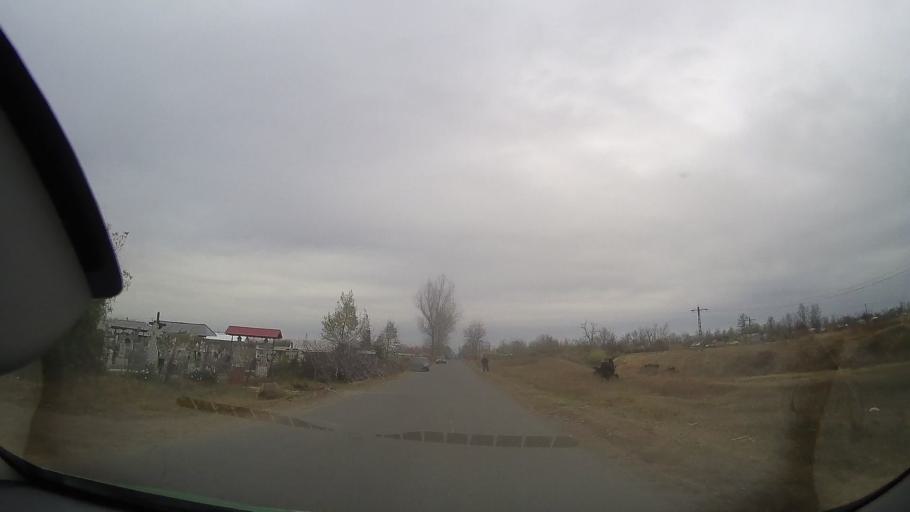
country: RO
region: Braila
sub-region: Comuna Rosiori
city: Rosiori
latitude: 44.8100
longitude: 27.3745
